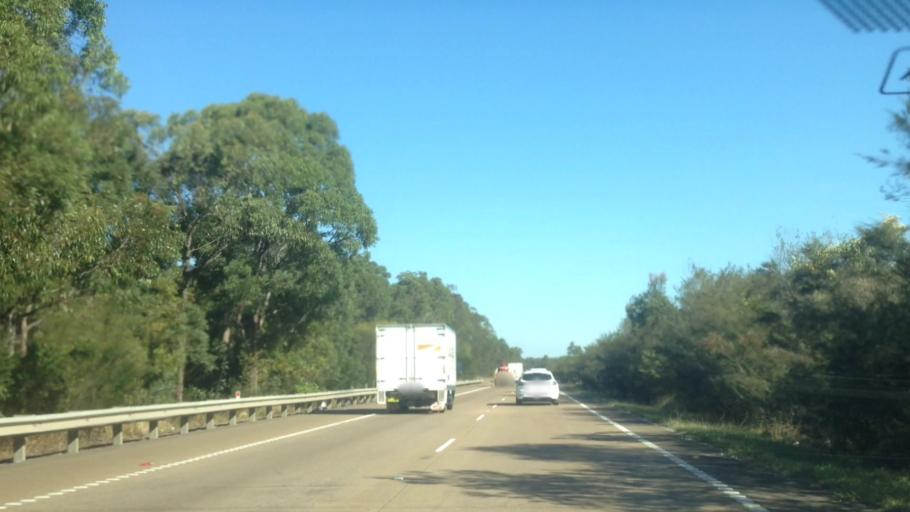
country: AU
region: New South Wales
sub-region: Wyong Shire
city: Charmhaven
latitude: -33.1589
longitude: 151.4702
